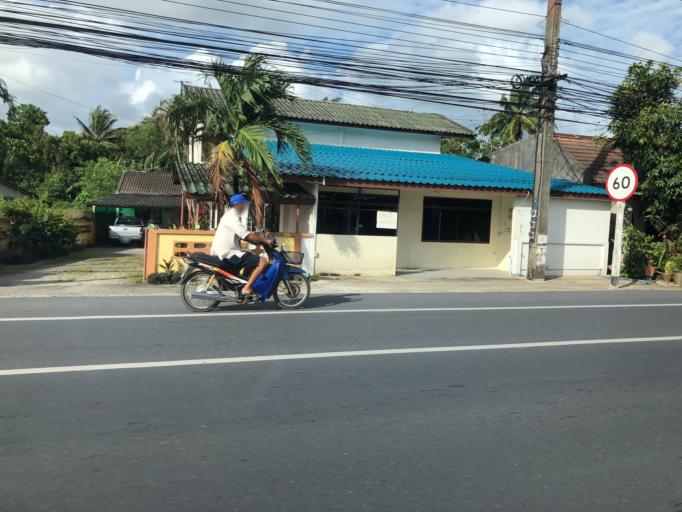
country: TH
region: Phuket
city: Thalang
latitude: 8.0012
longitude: 98.3473
